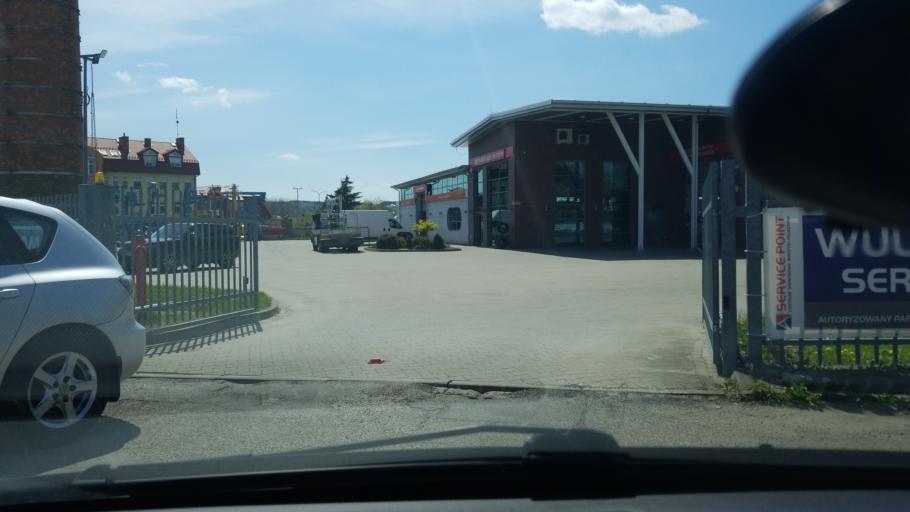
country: PL
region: Subcarpathian Voivodeship
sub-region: Powiat jasielski
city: Jaslo
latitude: 49.7397
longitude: 21.4844
